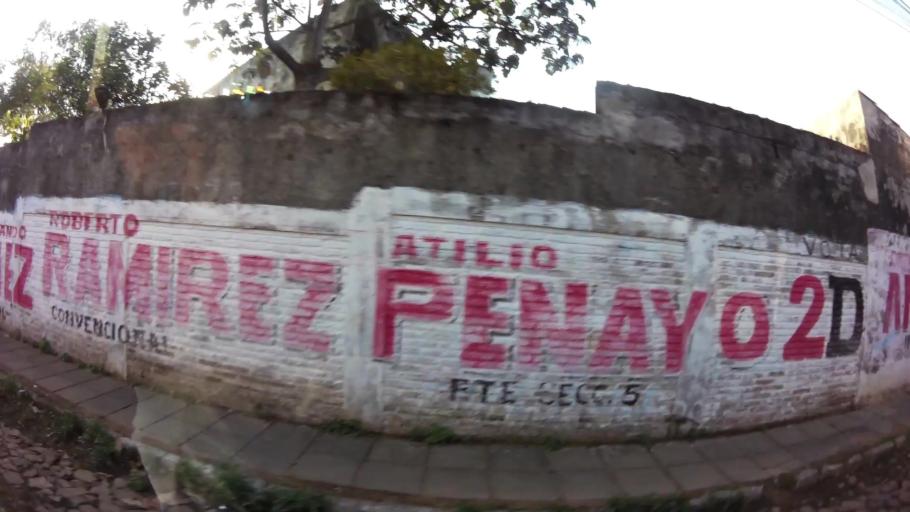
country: PY
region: Central
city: Lambare
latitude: -25.3447
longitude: -57.5963
